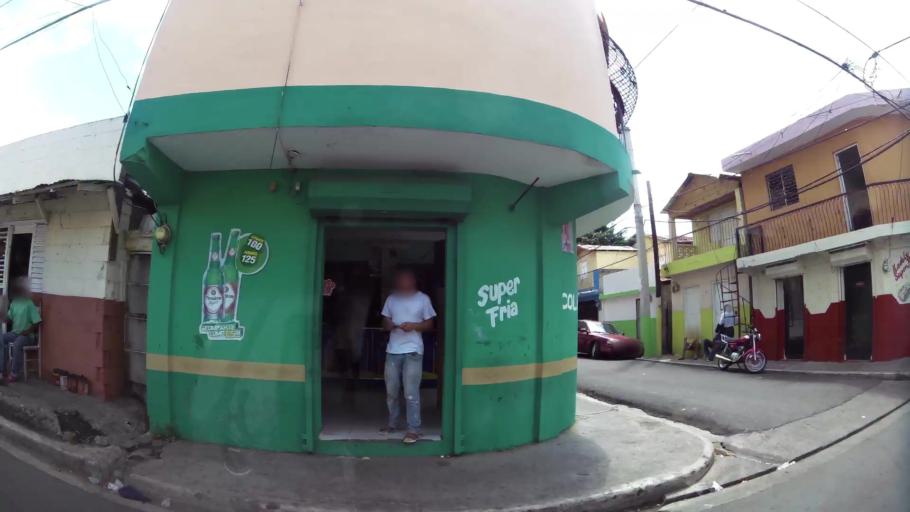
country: DO
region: Santiago
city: Santiago de los Caballeros
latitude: 19.4678
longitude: -70.7017
